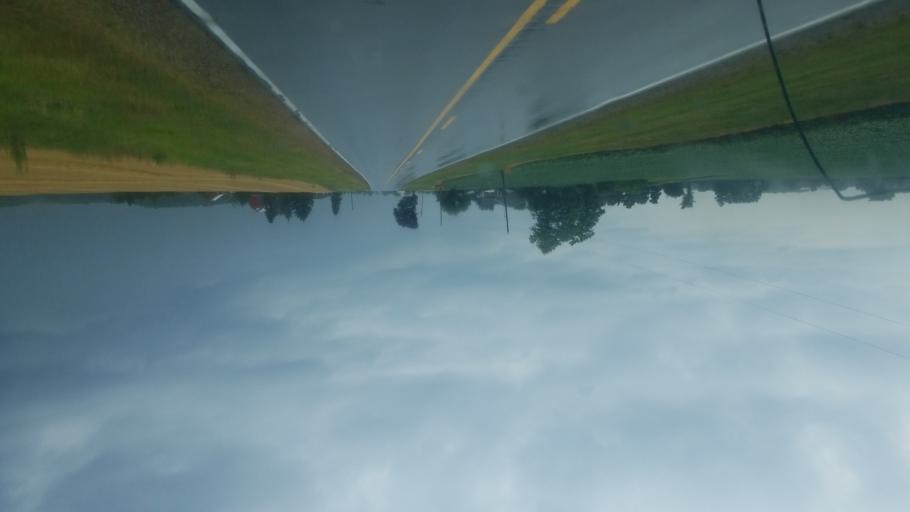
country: US
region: Indiana
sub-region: DeKalb County
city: Butler
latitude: 41.4805
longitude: -84.8724
